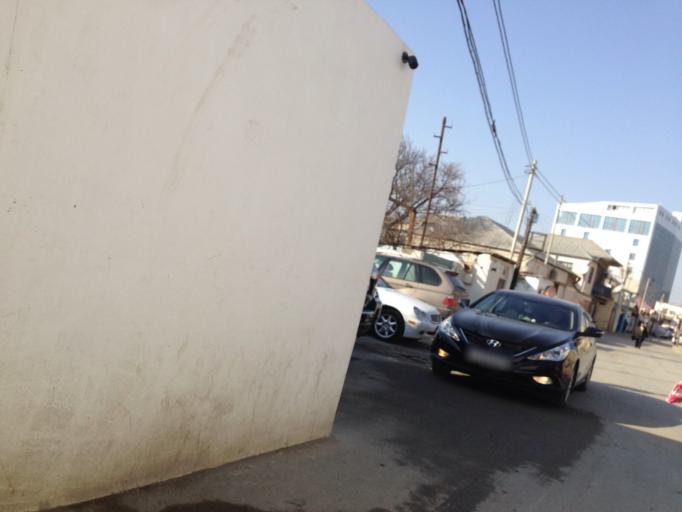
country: AZ
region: Baki
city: Baku
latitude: 40.3931
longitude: 49.8825
